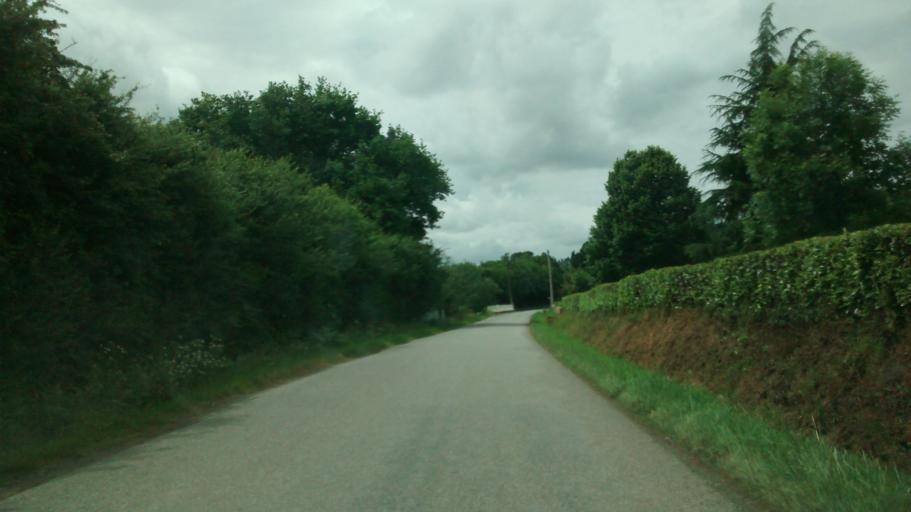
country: FR
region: Brittany
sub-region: Departement du Morbihan
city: Carentoir
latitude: 47.8240
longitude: -2.1614
